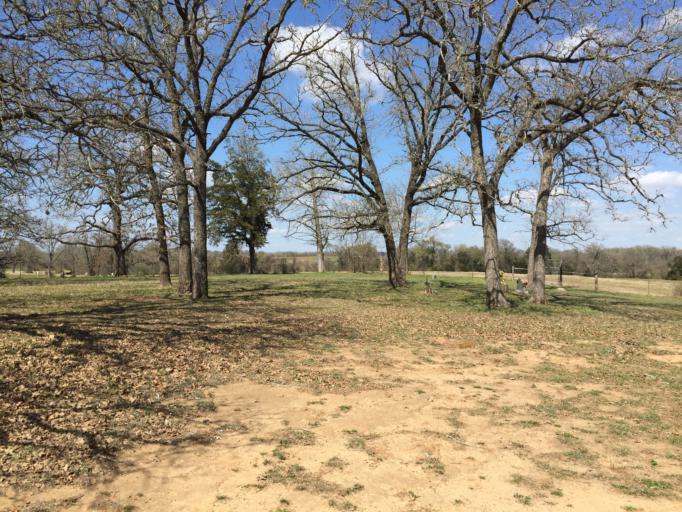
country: US
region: Texas
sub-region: Milam County
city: Thorndale
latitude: 30.5595
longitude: -97.1752
